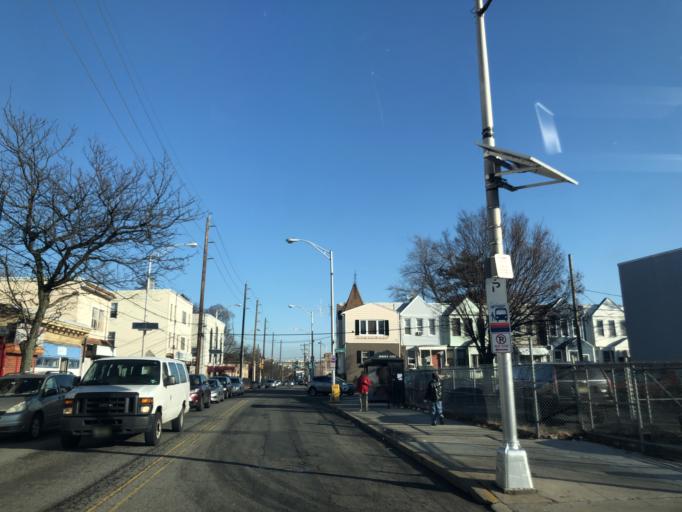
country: US
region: New Jersey
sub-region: Hudson County
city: Jersey City
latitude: 40.7271
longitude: -74.0763
